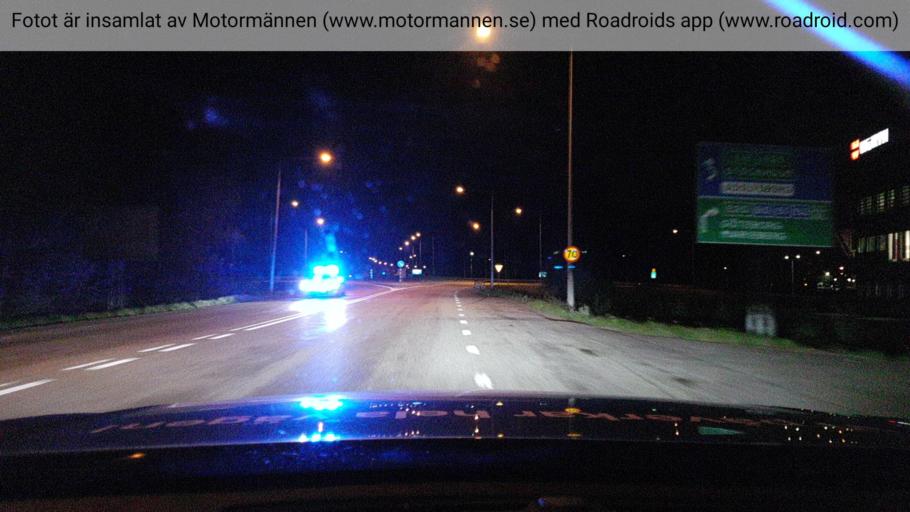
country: SE
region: OErebro
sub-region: Orebro Kommun
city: Orebro
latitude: 59.2394
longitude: 15.1416
